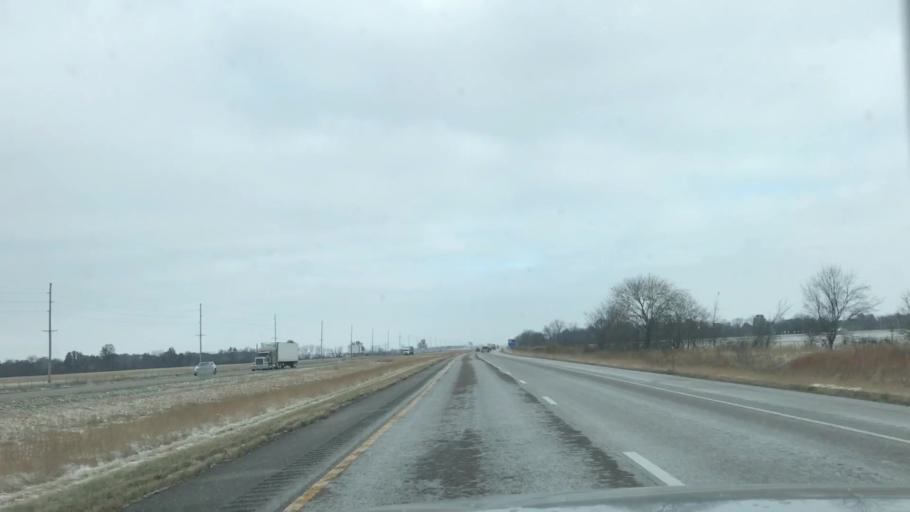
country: US
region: Illinois
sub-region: Macoupin County
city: Staunton
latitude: 38.9836
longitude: -89.7493
